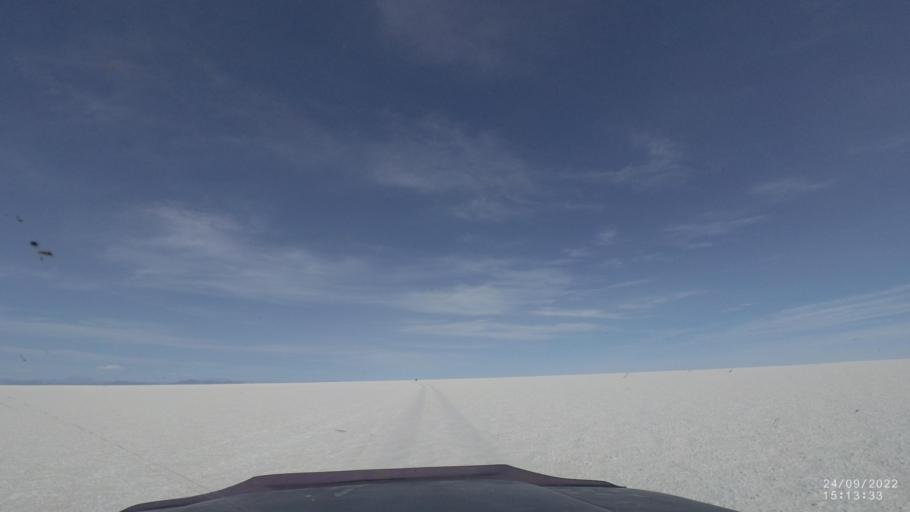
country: BO
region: Potosi
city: Colchani
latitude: -19.9565
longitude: -67.4644
